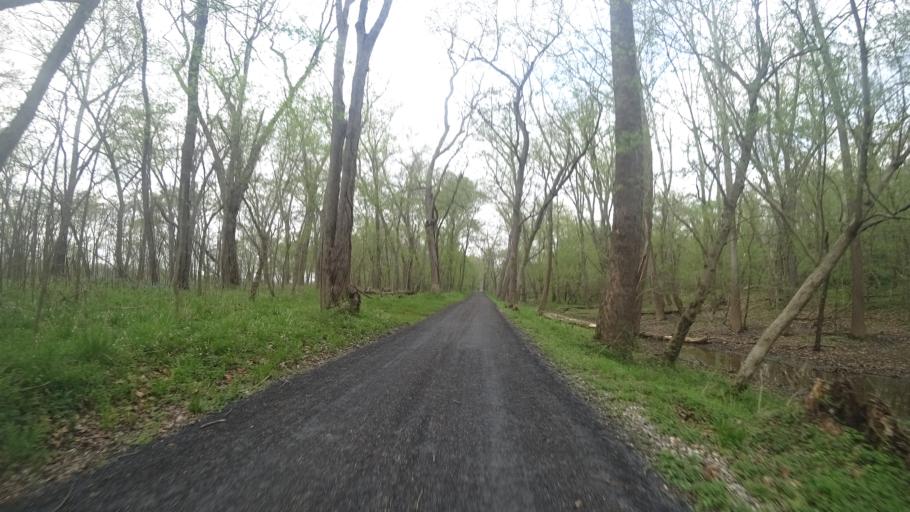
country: US
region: Virginia
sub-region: Loudoun County
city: University Center
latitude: 39.0997
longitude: -77.4714
